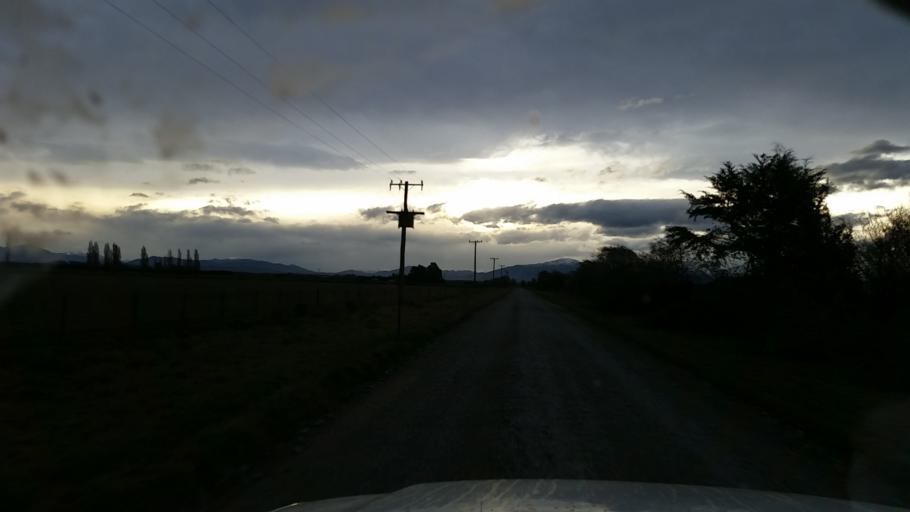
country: NZ
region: Canterbury
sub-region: Ashburton District
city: Ashburton
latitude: -43.8324
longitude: 171.6494
